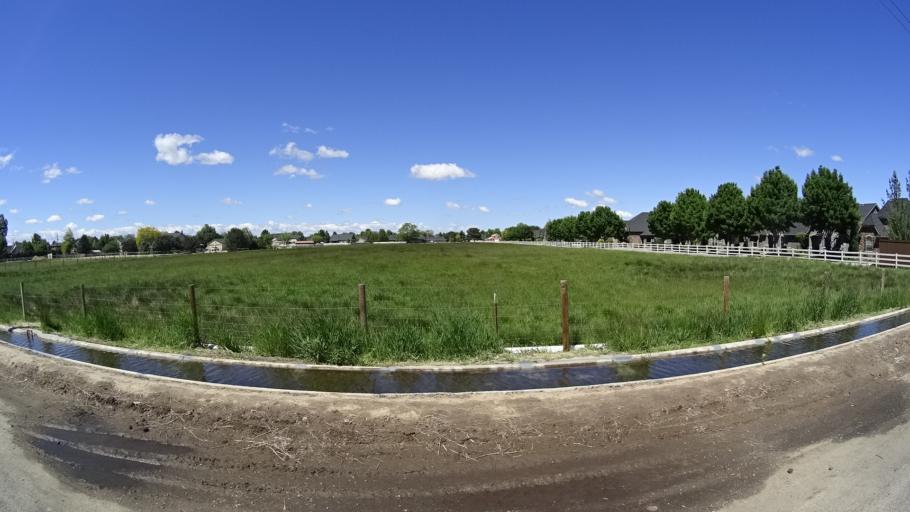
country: US
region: Idaho
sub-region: Ada County
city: Meridian
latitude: 43.6425
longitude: -116.3744
